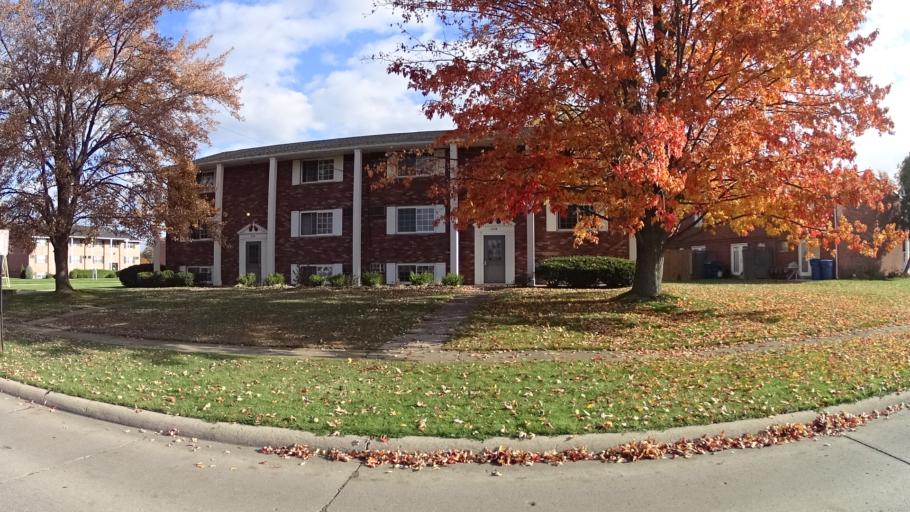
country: US
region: Ohio
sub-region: Lorain County
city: Lorain
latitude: 41.4340
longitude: -82.1828
